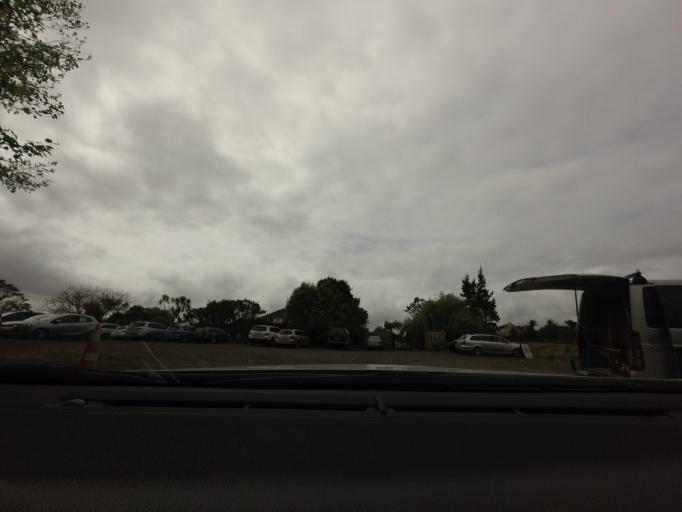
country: NZ
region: Auckland
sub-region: Auckland
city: Waitakere
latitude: -36.8967
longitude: 174.6010
